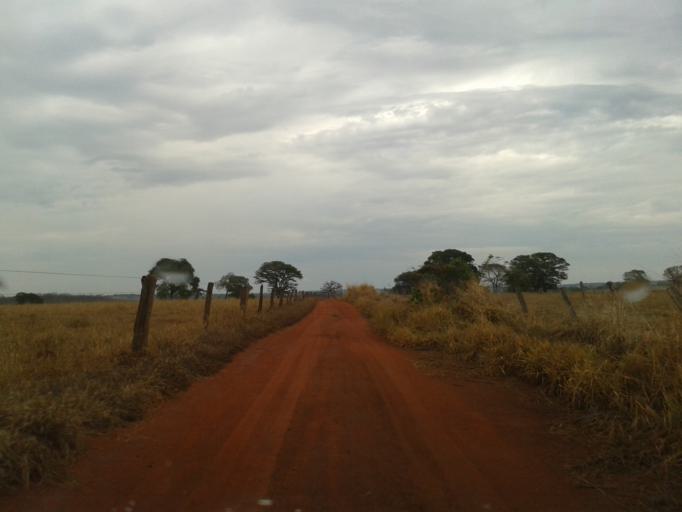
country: BR
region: Minas Gerais
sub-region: Capinopolis
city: Capinopolis
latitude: -18.8716
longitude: -49.8075
